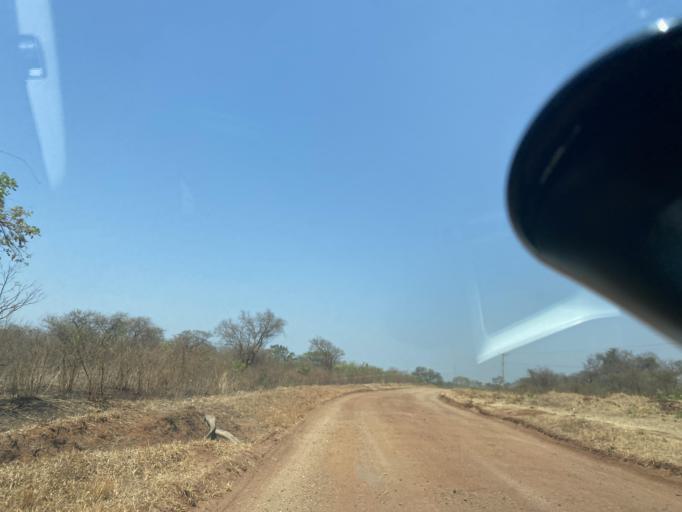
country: ZM
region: Lusaka
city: Lusaka
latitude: -15.5238
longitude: 28.1084
